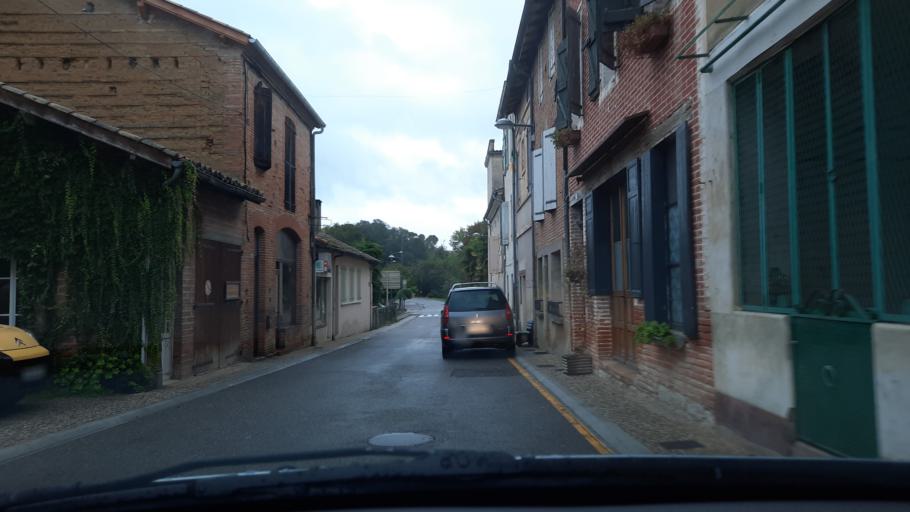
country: FR
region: Midi-Pyrenees
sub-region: Departement du Tarn-et-Garonne
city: Lafrancaise
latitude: 44.1897
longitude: 1.2853
